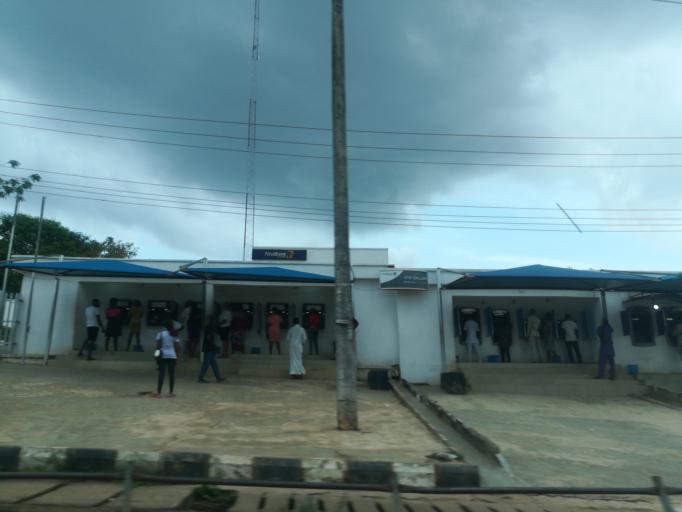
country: NG
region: Oyo
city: Ibadan
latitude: 7.4277
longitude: 3.8943
